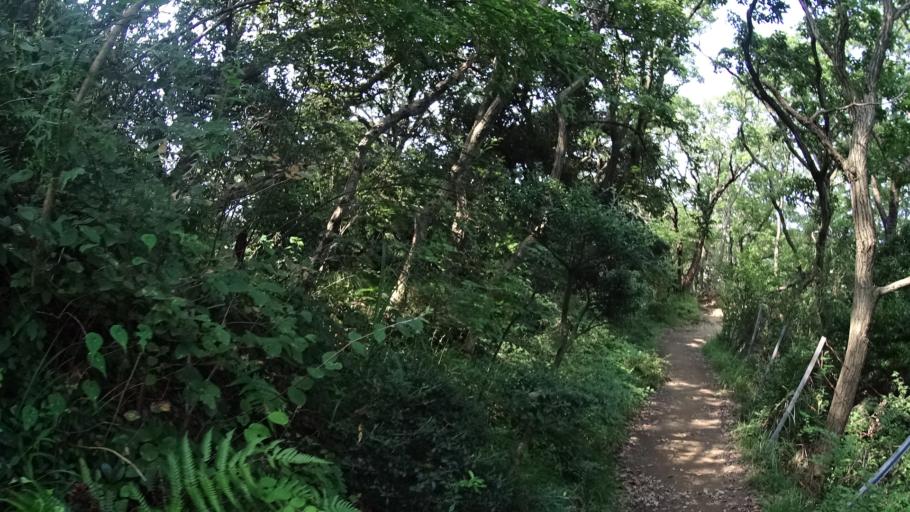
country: JP
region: Kanagawa
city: Zushi
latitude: 35.3064
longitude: 139.6093
